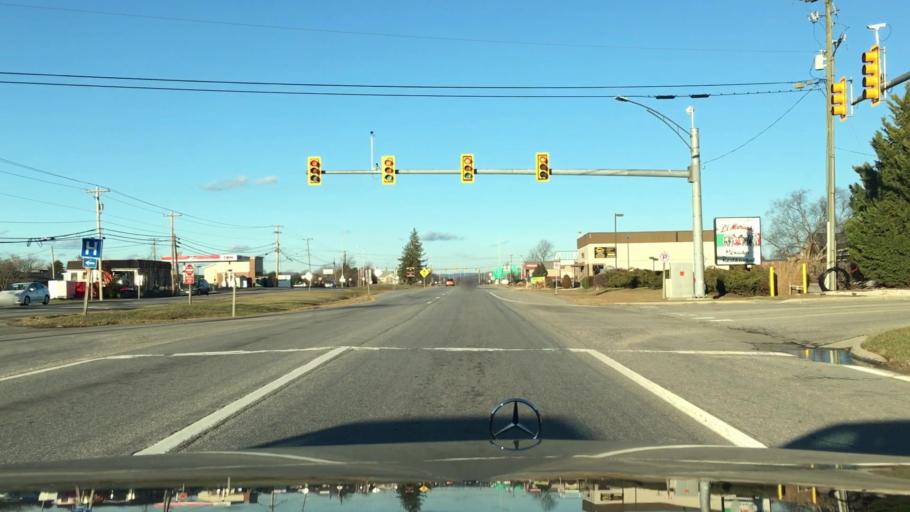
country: US
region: Virginia
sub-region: Montgomery County
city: Merrimac
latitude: 37.1853
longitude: -80.4085
